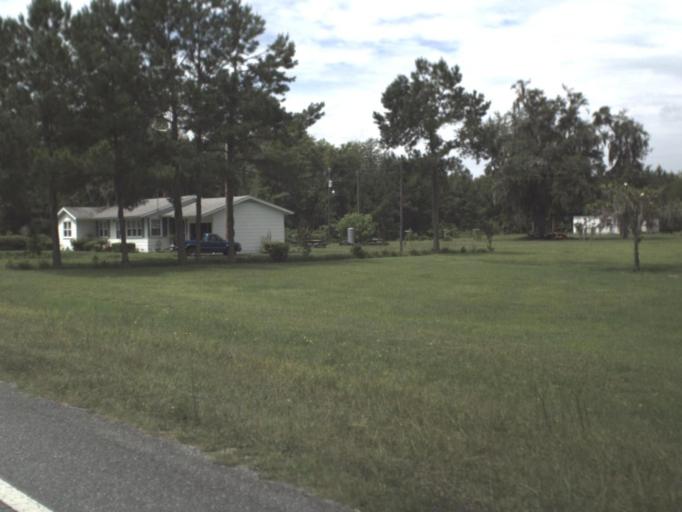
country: US
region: Florida
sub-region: Suwannee County
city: Live Oak
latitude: 30.3671
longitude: -82.9413
